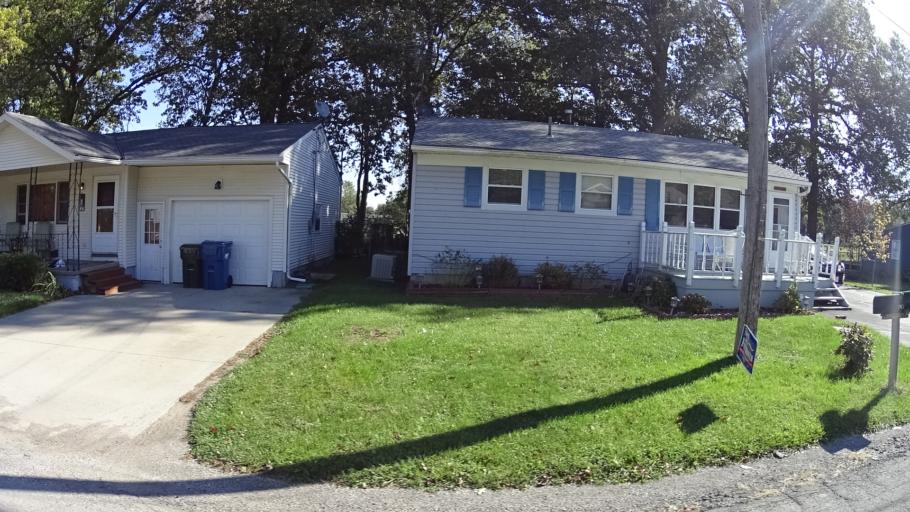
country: US
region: Ohio
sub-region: Lorain County
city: Vermilion-on-the-Lake
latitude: 41.4288
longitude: -82.3151
